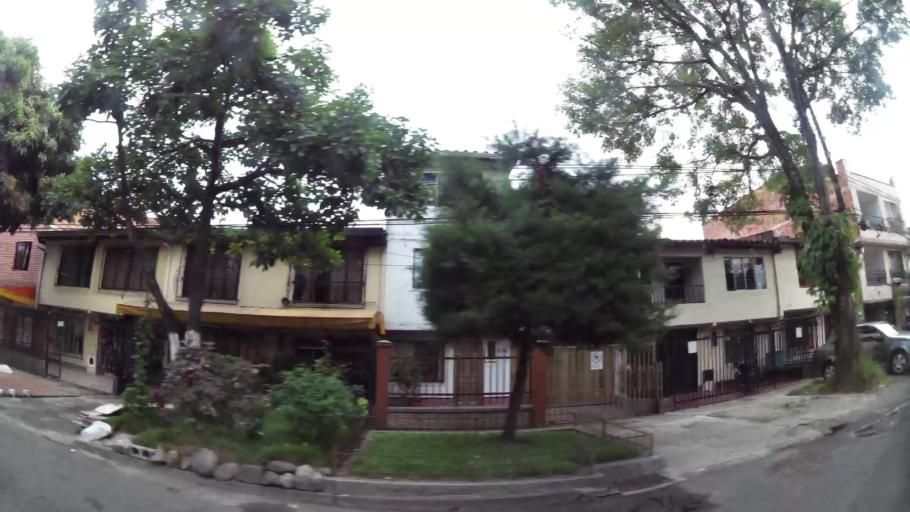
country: CO
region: Antioquia
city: Itagui
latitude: 6.2102
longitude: -75.5875
